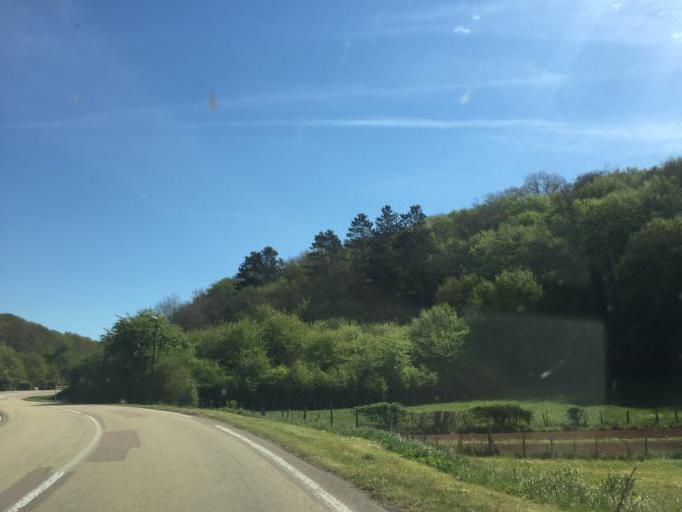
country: FR
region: Bourgogne
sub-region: Departement de la Nievre
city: Clamecy
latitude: 47.4568
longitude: 3.6667
